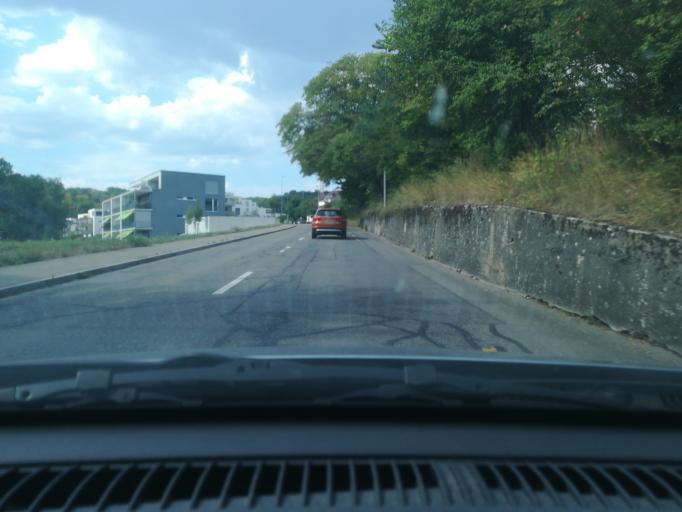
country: CH
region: Schaffhausen
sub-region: Bezirk Reiat
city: Stetten
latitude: 47.7259
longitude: 8.6639
